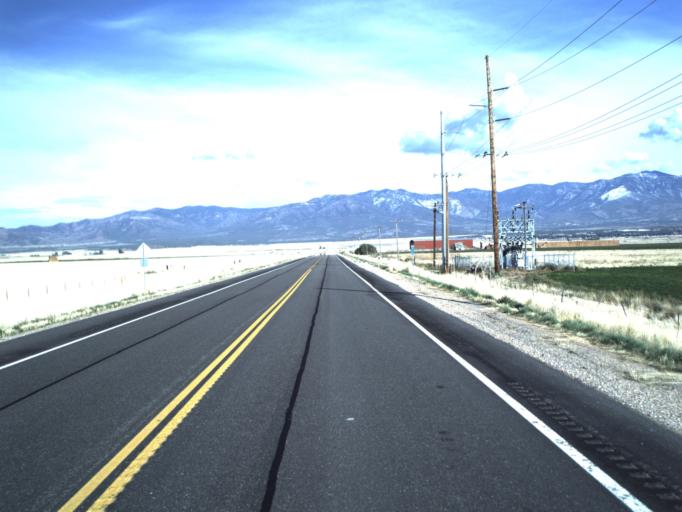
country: US
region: Utah
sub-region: Millard County
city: Fillmore
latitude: 39.1181
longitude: -112.3501
